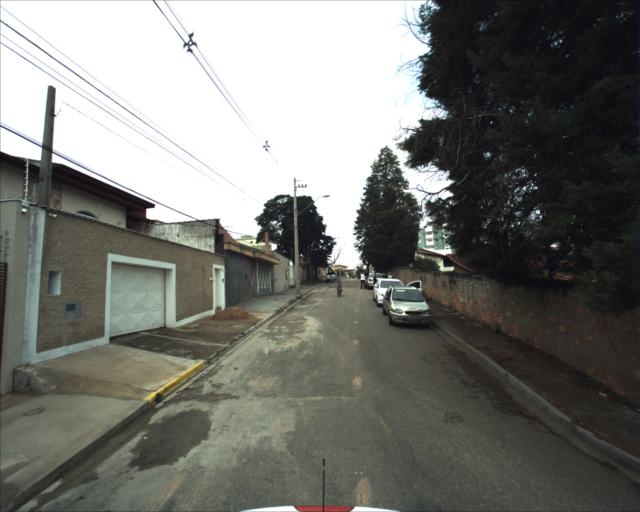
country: BR
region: Sao Paulo
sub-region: Sorocaba
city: Sorocaba
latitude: -23.5070
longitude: -47.4973
